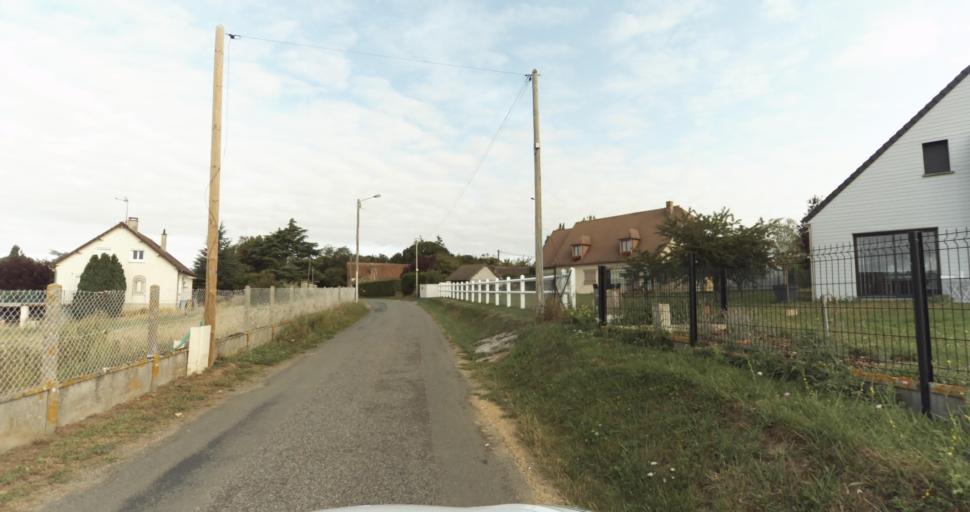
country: FR
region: Haute-Normandie
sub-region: Departement de l'Eure
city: Saint-Germain-sur-Avre
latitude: 48.8179
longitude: 1.2711
